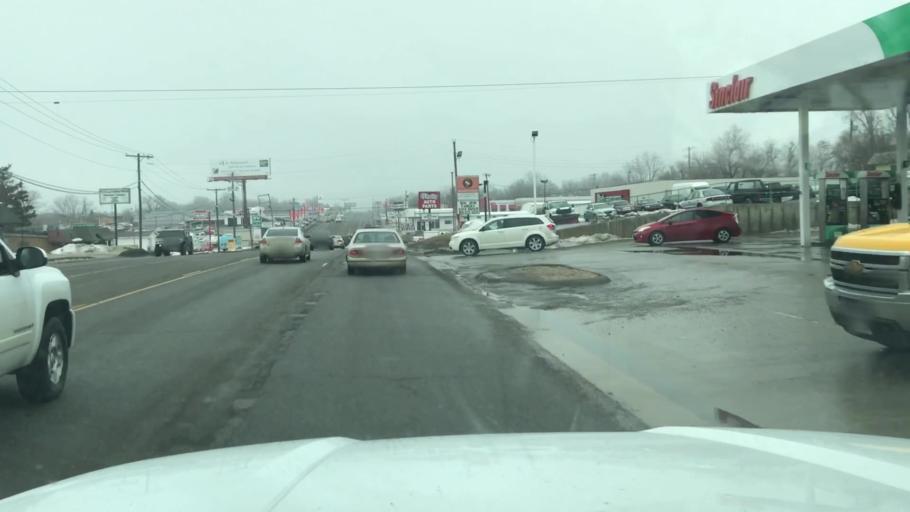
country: US
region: Missouri
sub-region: Buchanan County
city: Saint Joseph
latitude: 39.7570
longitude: -94.8037
